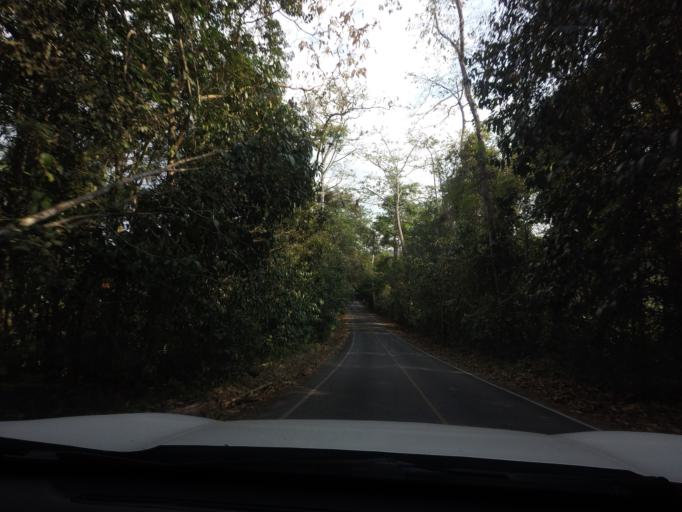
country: TH
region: Nakhon Ratchasima
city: Pak Chong
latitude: 14.4343
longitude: 101.4116
